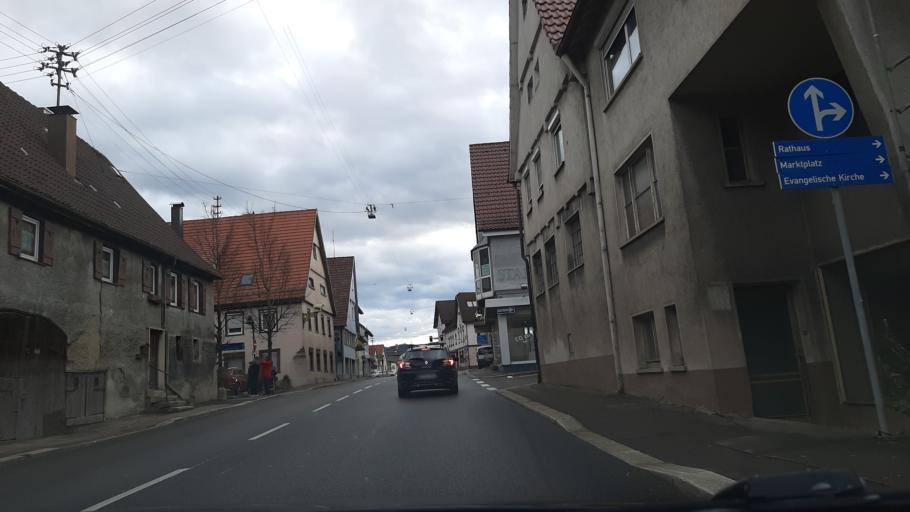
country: DE
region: Baden-Wuerttemberg
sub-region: Regierungsbezirk Stuttgart
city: Kuchen
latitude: 48.6367
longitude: 9.7980
